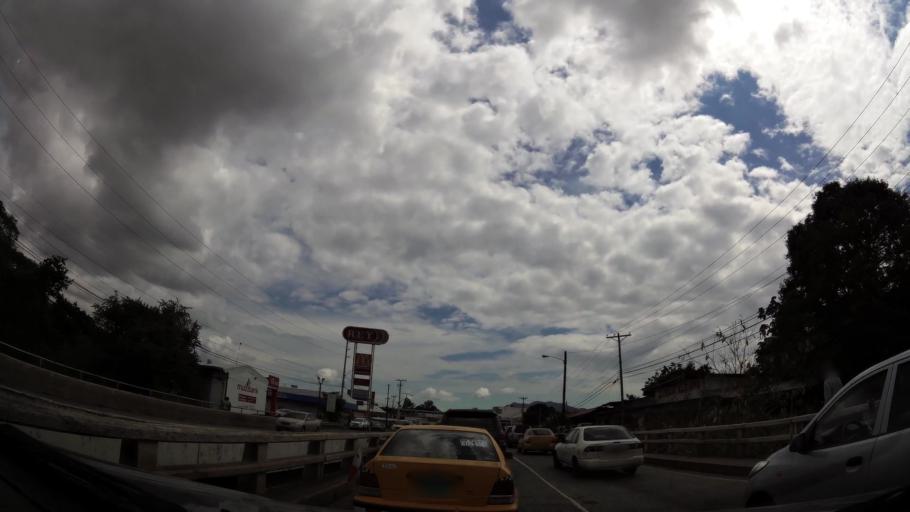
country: PA
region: Panama
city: Nuevo Arraijan
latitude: 8.9255
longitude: -79.7129
